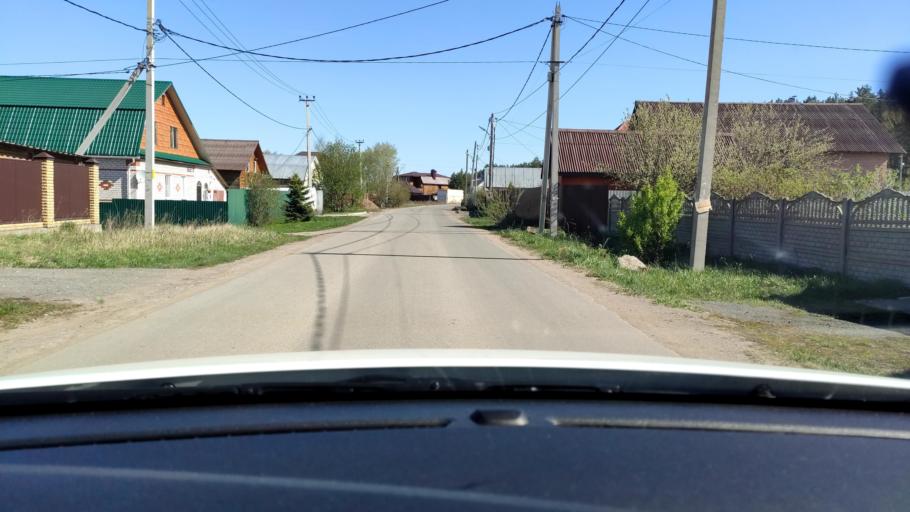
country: RU
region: Tatarstan
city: Vysokaya Gora
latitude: 55.8774
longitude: 49.2467
